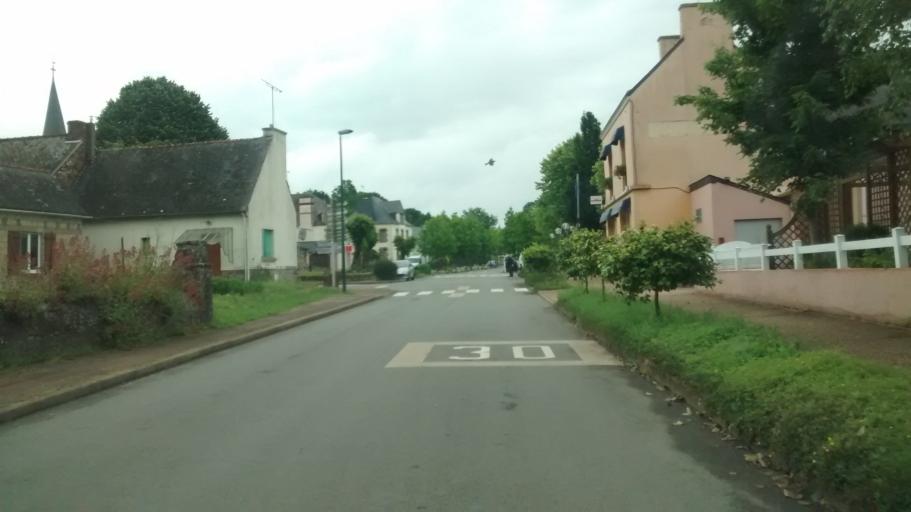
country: FR
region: Brittany
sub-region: Departement du Morbihan
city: Malestroit
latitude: 47.8039
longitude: -2.4197
